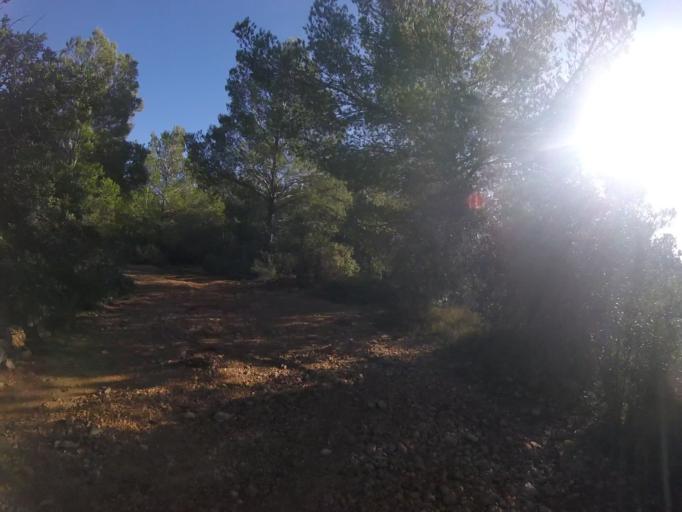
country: ES
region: Valencia
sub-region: Provincia de Castello
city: Sarratella
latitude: 40.2857
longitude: 0.0638
